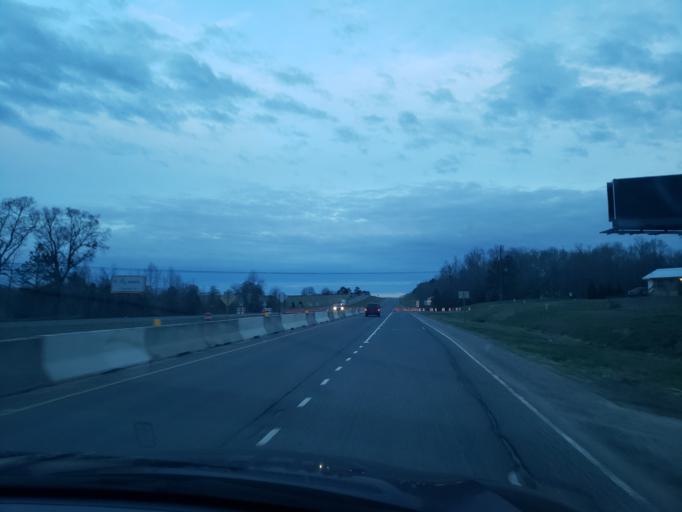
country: US
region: Alabama
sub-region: Lee County
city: Auburn
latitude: 32.6798
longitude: -85.4898
